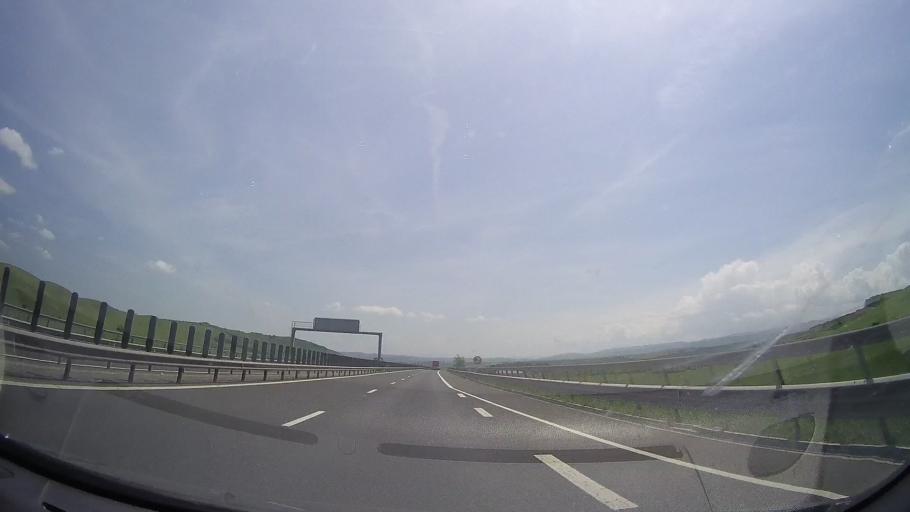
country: RO
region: Alba
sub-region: Comuna Garbova
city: Garbova
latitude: 45.9153
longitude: 23.7302
